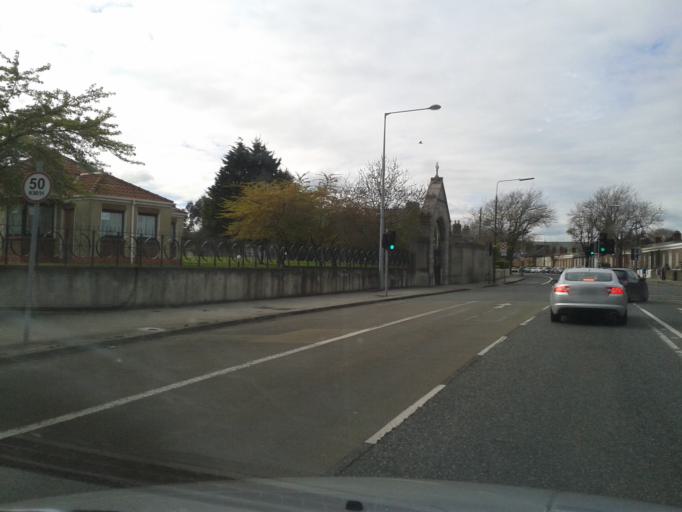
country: IE
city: Booterstown
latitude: 53.3159
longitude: -6.2048
